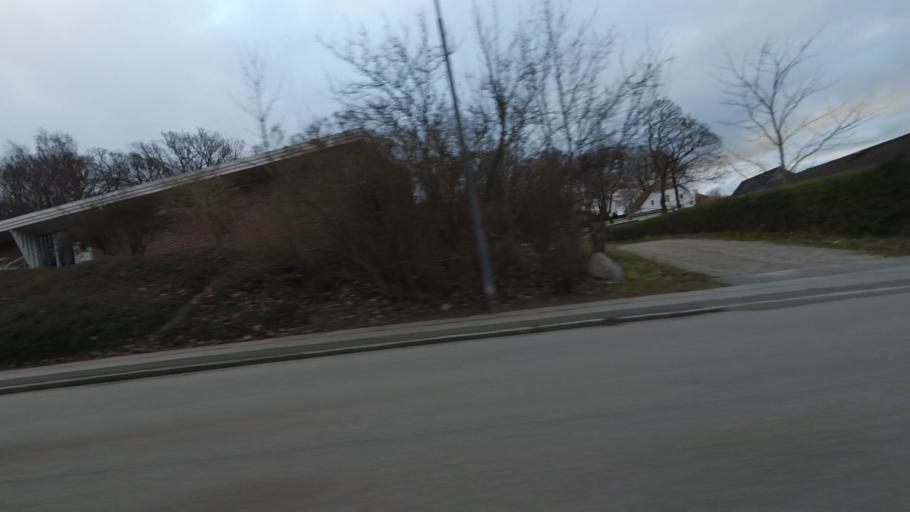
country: DK
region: Central Jutland
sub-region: Arhus Kommune
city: Stavtrup
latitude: 56.1573
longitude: 10.1017
